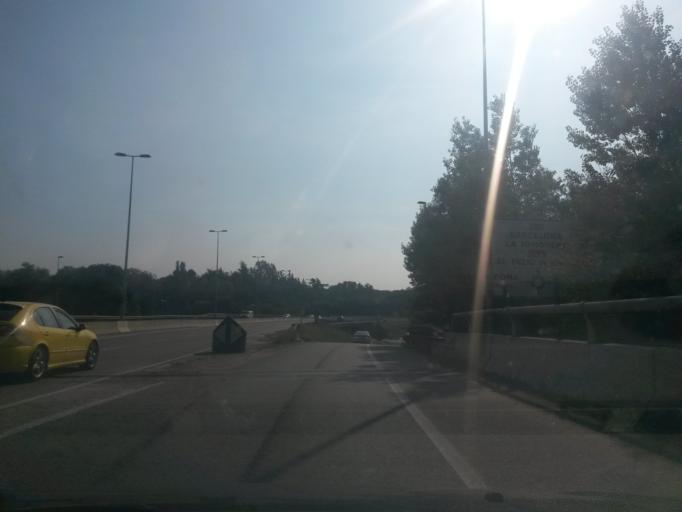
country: ES
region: Catalonia
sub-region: Provincia de Girona
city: Salt
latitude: 41.9571
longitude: 2.8082
